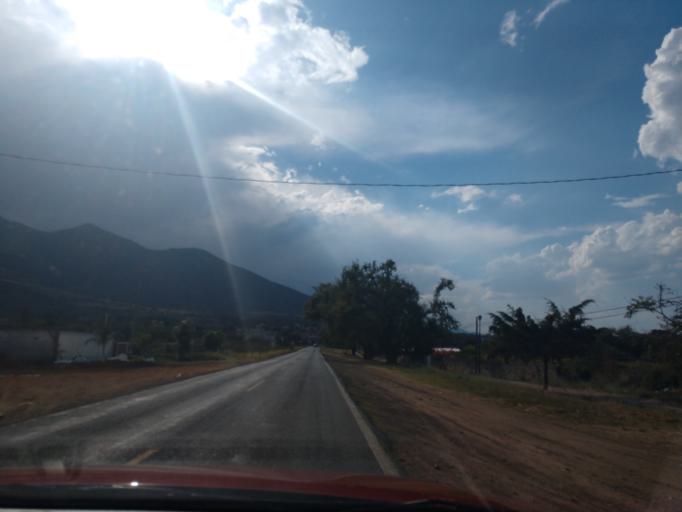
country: MX
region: Jalisco
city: San Juan Cosala
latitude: 20.1944
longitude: -103.2992
